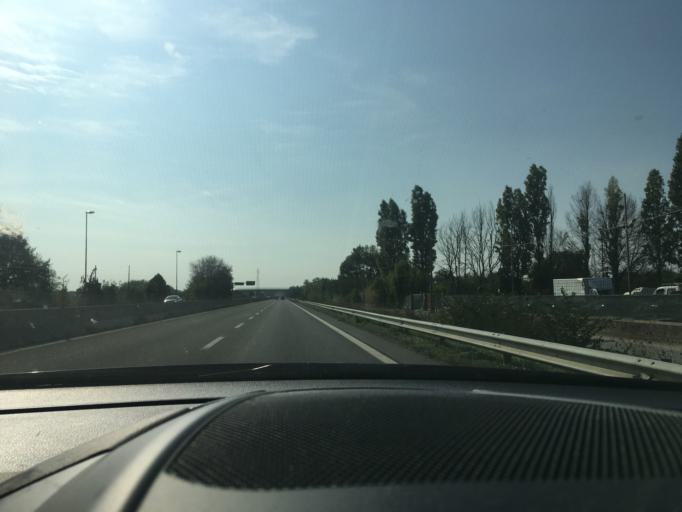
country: IT
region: Emilia-Romagna
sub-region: Provincia di Rimini
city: Bellaria-Igea Marina
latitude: 44.1401
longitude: 12.4590
